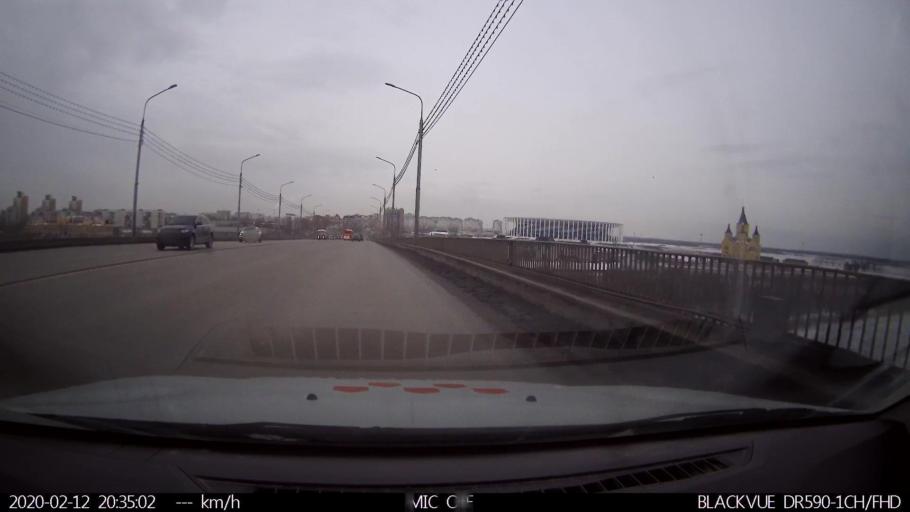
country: RU
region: Nizjnij Novgorod
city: Nizhniy Novgorod
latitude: 56.3307
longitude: 43.9737
